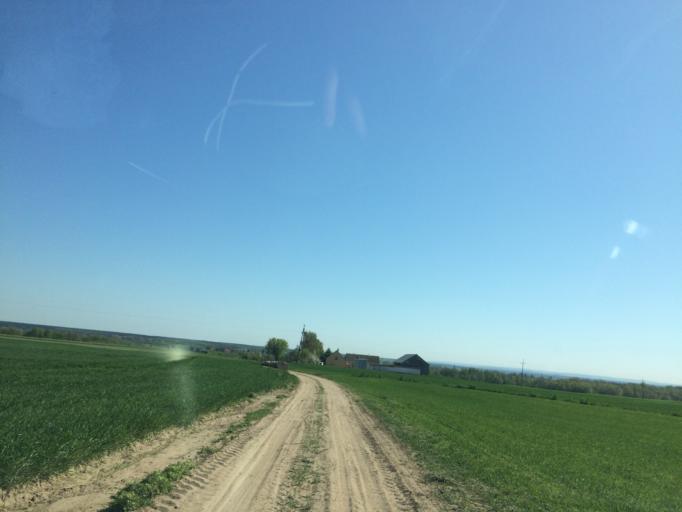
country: PL
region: Warmian-Masurian Voivodeship
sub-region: Powiat nowomiejski
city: Nowe Miasto Lubawskie
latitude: 53.4922
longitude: 19.5049
